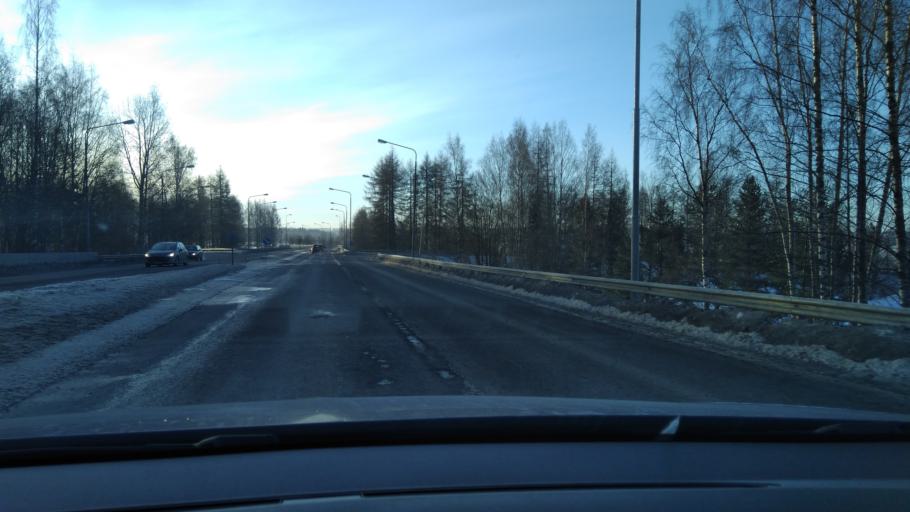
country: FI
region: Pirkanmaa
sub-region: Tampere
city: Pirkkala
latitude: 61.4992
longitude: 23.6514
